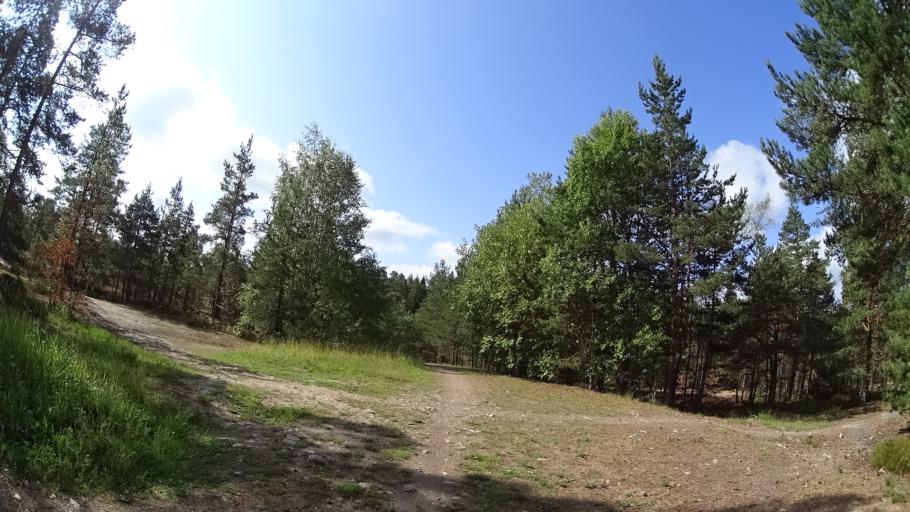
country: FI
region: Uusimaa
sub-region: Helsinki
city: Teekkarikylae
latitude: 60.2922
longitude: 24.9037
